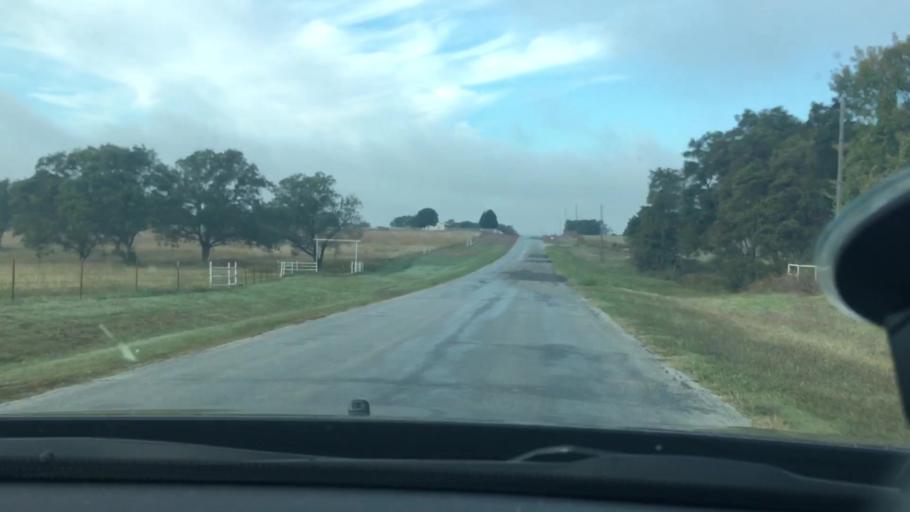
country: US
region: Oklahoma
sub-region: Murray County
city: Sulphur
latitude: 34.6223
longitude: -96.9528
